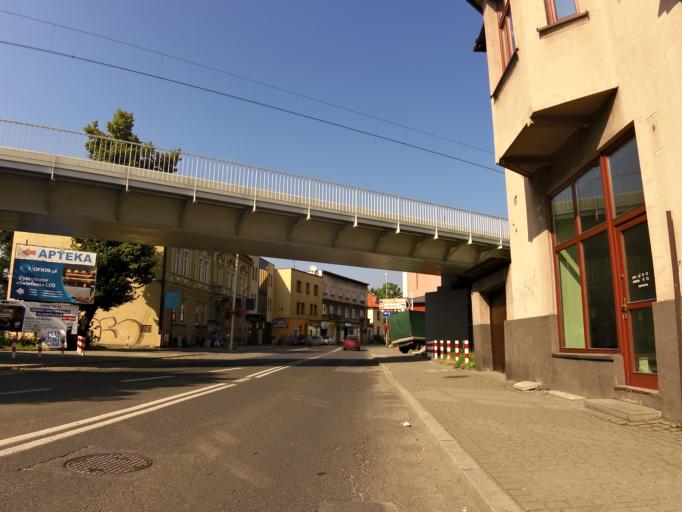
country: PL
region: Silesian Voivodeship
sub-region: Powiat zywiecki
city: Zywiec
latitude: 49.6835
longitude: 19.1902
